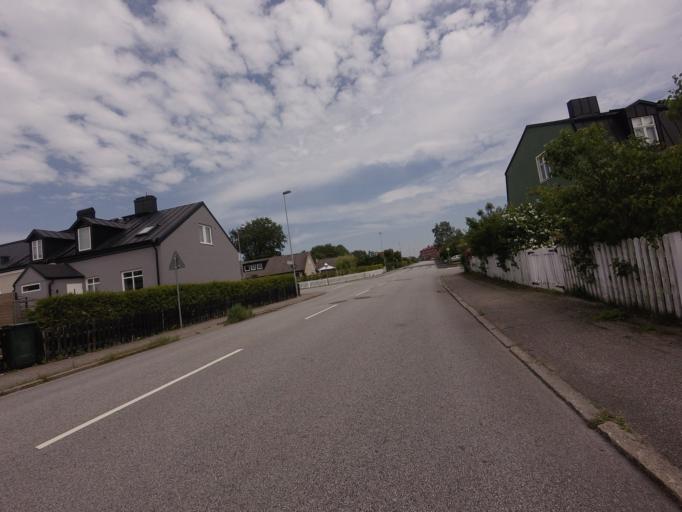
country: SE
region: Skane
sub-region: Ystads Kommun
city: Ystad
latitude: 55.4288
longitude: 13.8001
